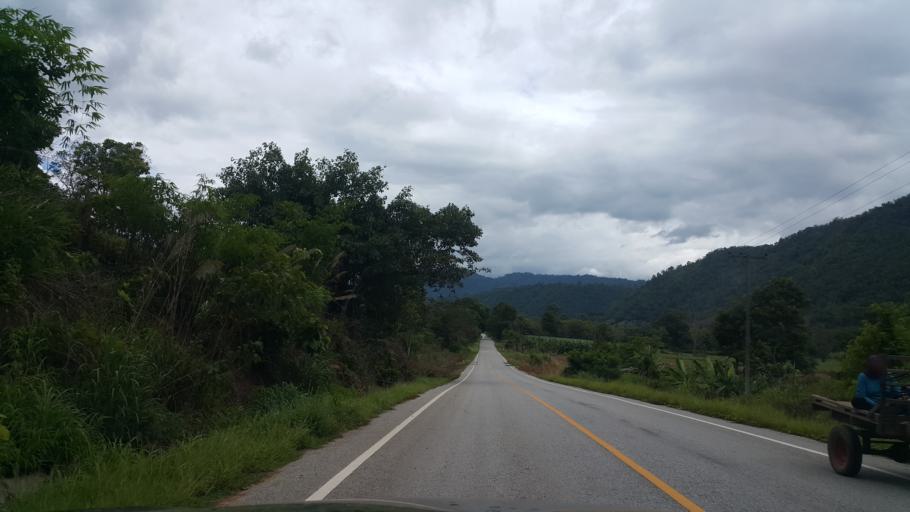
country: TH
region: Phitsanulok
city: Chat Trakan
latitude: 17.3722
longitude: 100.7424
